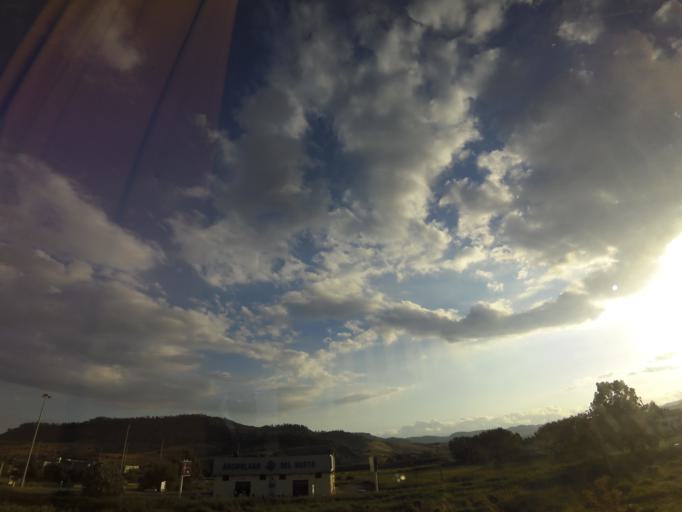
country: IT
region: Calabria
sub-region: Provincia di Catanzaro
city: Catanzaro
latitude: 38.8592
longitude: 16.5709
